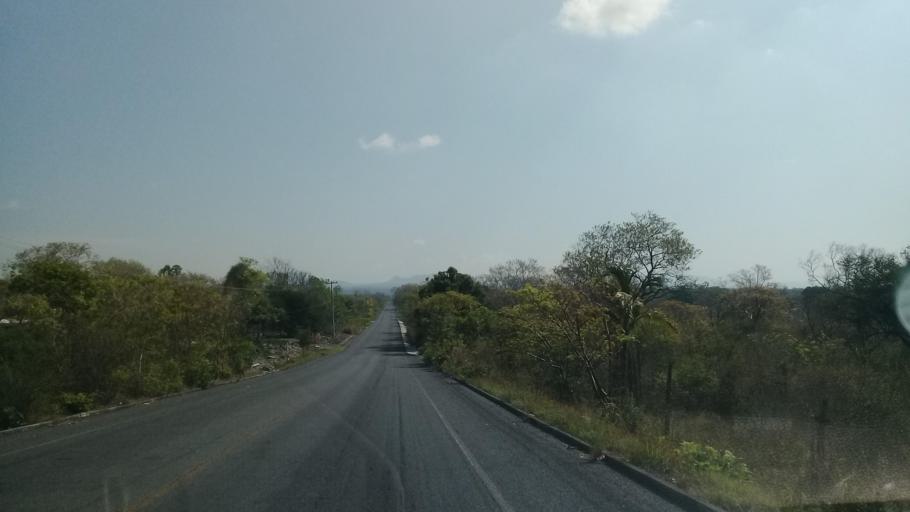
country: MX
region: Veracruz
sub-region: Emiliano Zapata
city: Plan del Rio
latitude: 19.3962
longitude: -96.6178
